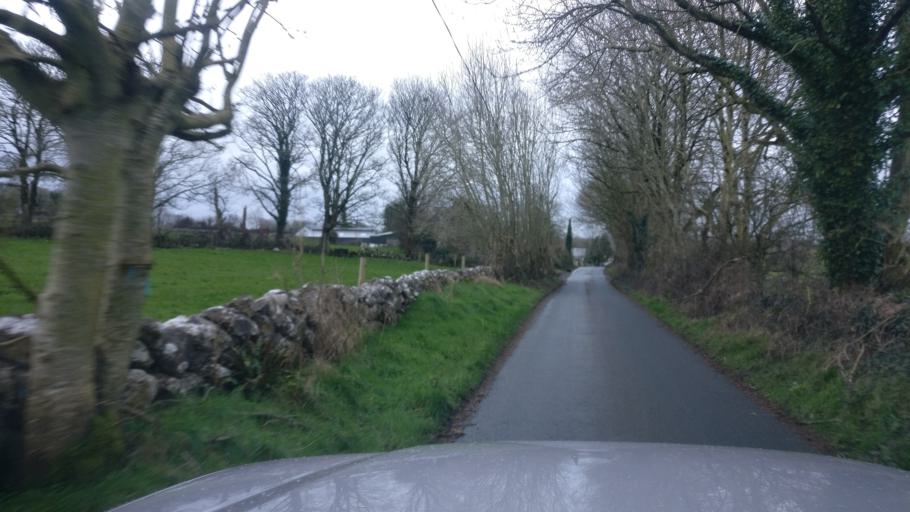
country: IE
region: Connaught
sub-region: County Galway
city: Athenry
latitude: 53.1849
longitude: -8.7186
